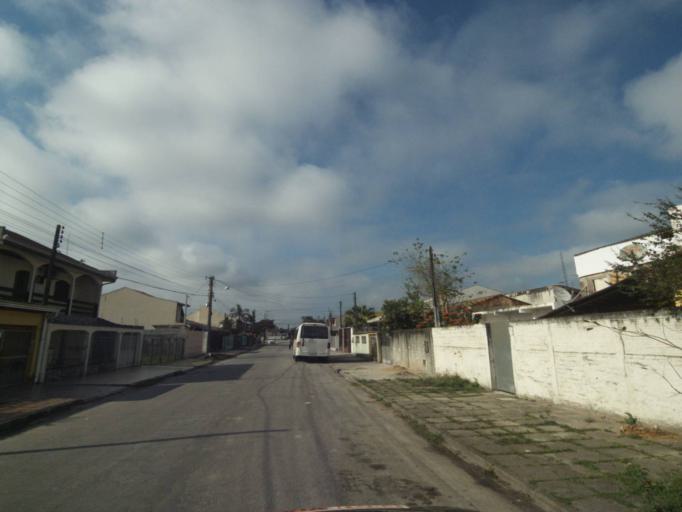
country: BR
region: Parana
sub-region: Paranagua
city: Paranagua
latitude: -25.5580
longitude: -48.5602
